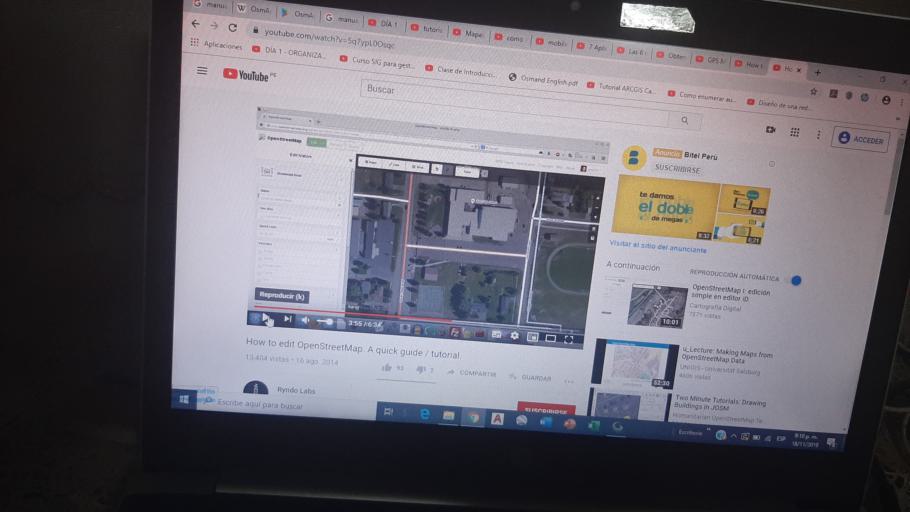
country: PE
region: Cusco
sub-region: Provincia de Cusco
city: Cusco
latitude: -13.5395
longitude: -71.9248
